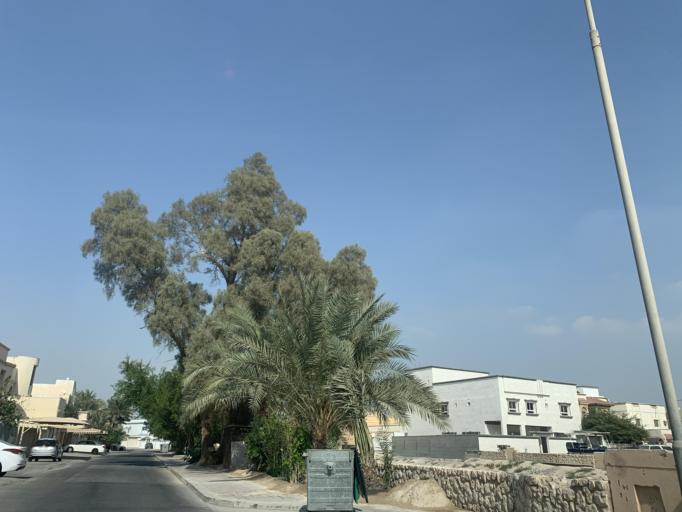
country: BH
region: Central Governorate
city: Madinat Hamad
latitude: 26.1257
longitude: 50.4914
